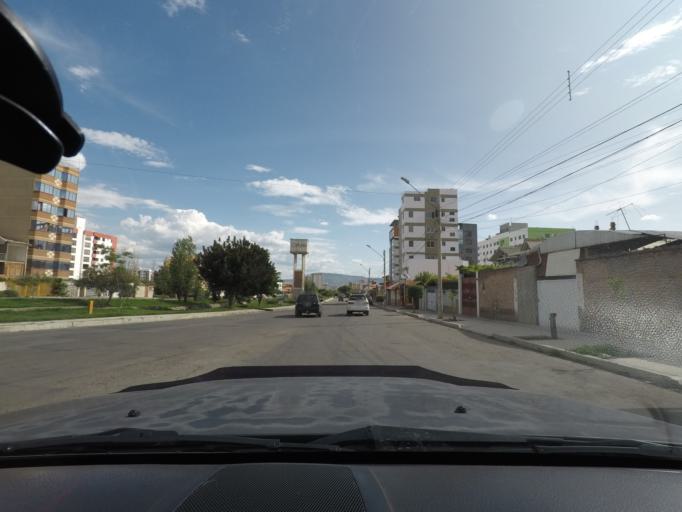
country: BO
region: Cochabamba
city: Cochabamba
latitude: -17.3737
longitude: -66.1821
